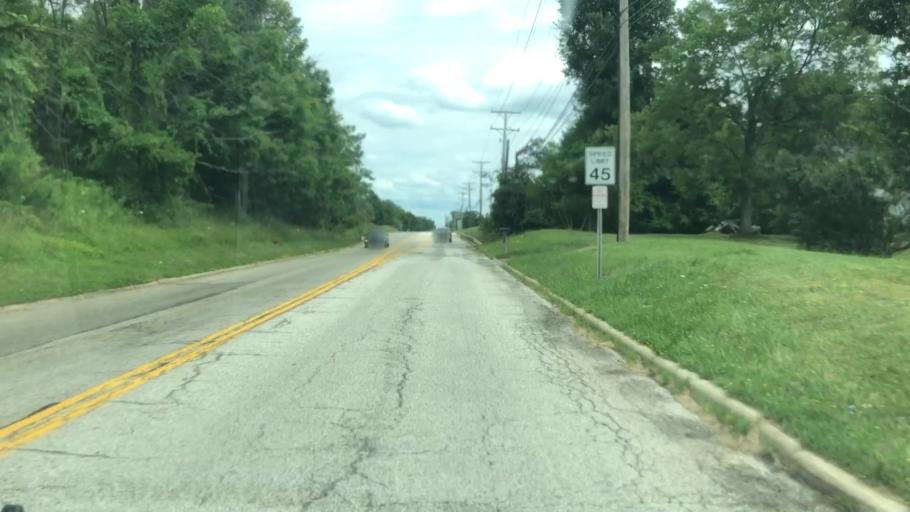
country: US
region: Ohio
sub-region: Summit County
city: Peninsula
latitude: 41.1809
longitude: -81.5554
